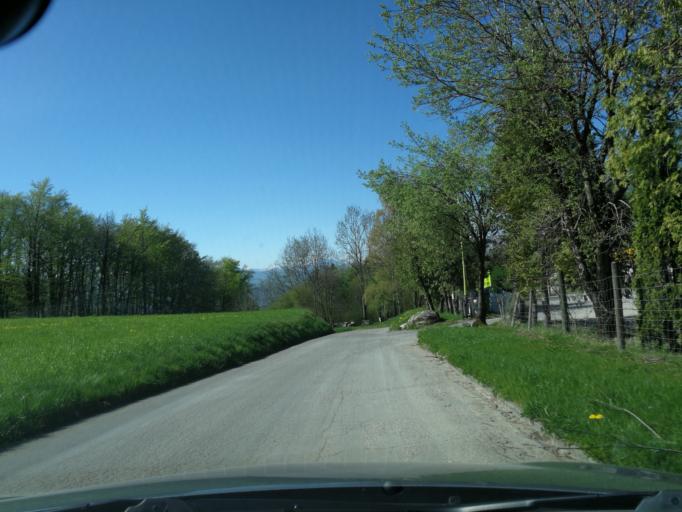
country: CH
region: Zurich
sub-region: Bezirk Meilen
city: Uetikon / Grossdorf
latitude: 47.2779
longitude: 8.6729
